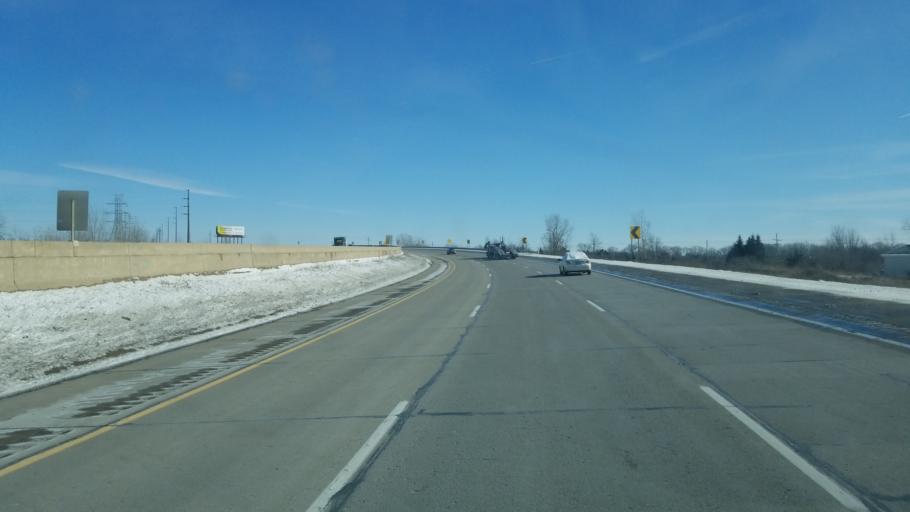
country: US
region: Michigan
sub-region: Livingston County
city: Howell
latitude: 42.5787
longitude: -83.8904
